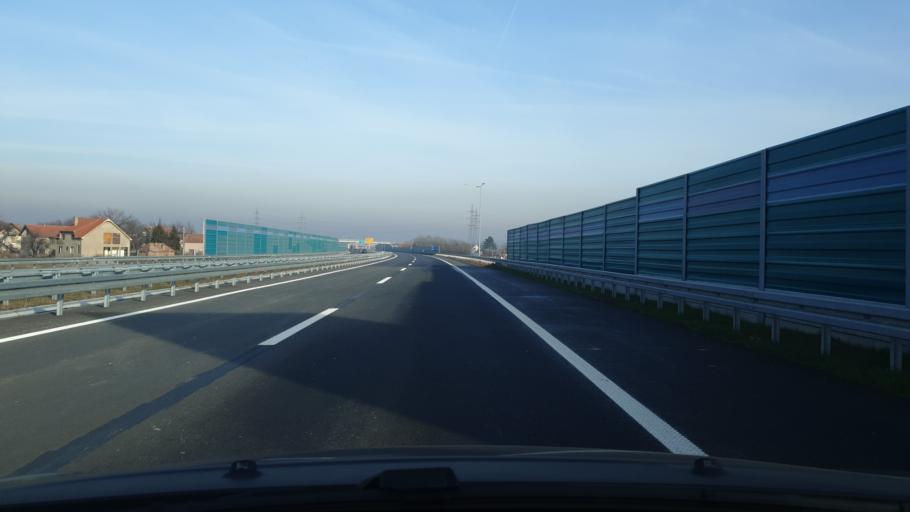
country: RS
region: Central Serbia
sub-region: Belgrade
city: Obrenovac
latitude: 44.6473
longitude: 20.2232
